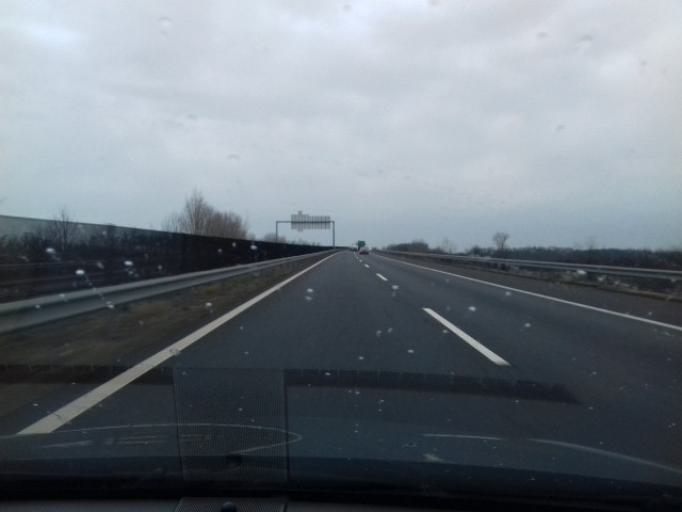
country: HU
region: Szabolcs-Szatmar-Bereg
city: Nagykallo
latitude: 47.8902
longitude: 21.7868
